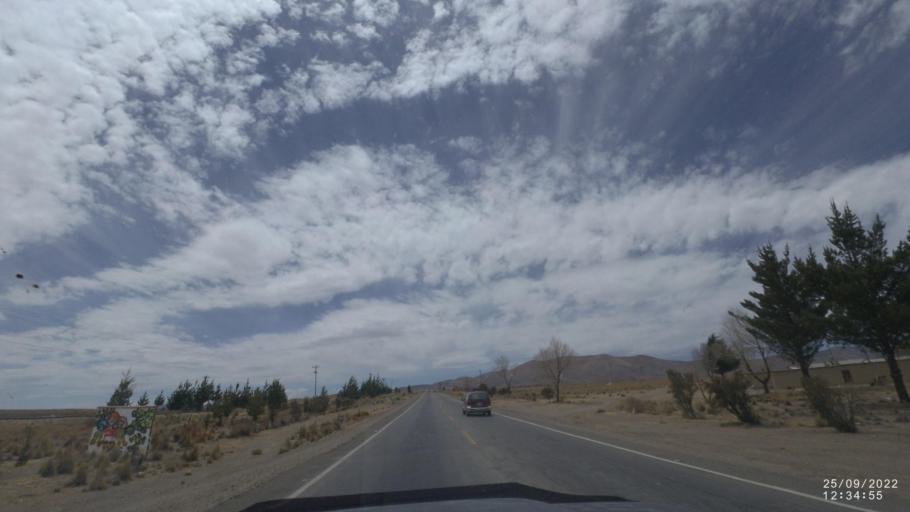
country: BO
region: Oruro
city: Machacamarca
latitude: -18.1677
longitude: -67.0106
